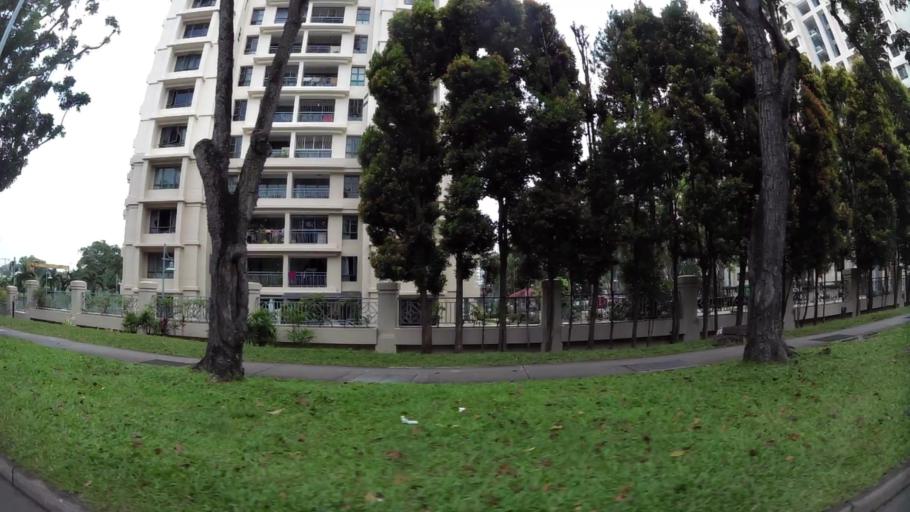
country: SG
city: Singapore
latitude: 1.3390
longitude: 103.9352
